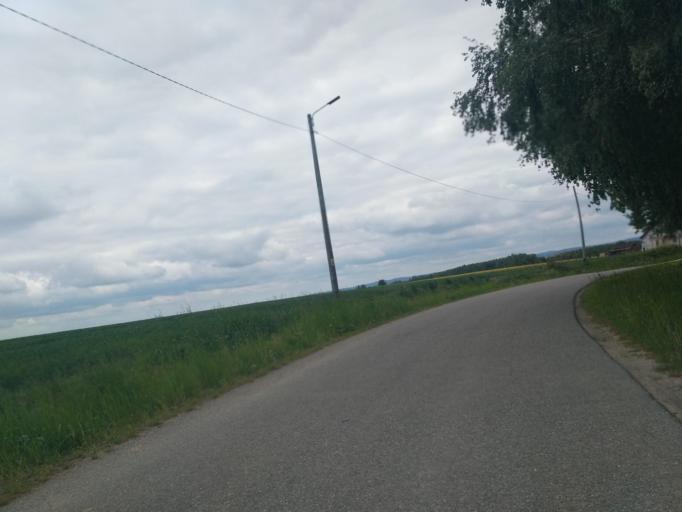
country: PL
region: Subcarpathian Voivodeship
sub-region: Powiat jasielski
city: Tarnowiec
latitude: 49.6953
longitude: 21.5811
